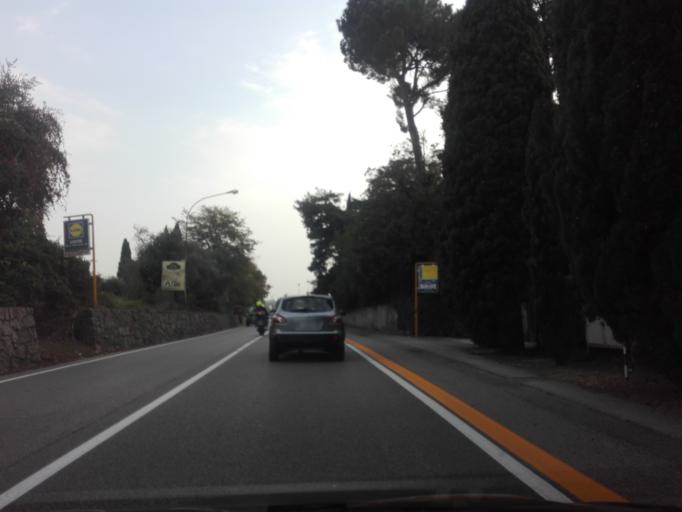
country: IT
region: Veneto
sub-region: Provincia di Verona
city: Lazise
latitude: 45.5141
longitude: 10.7317
